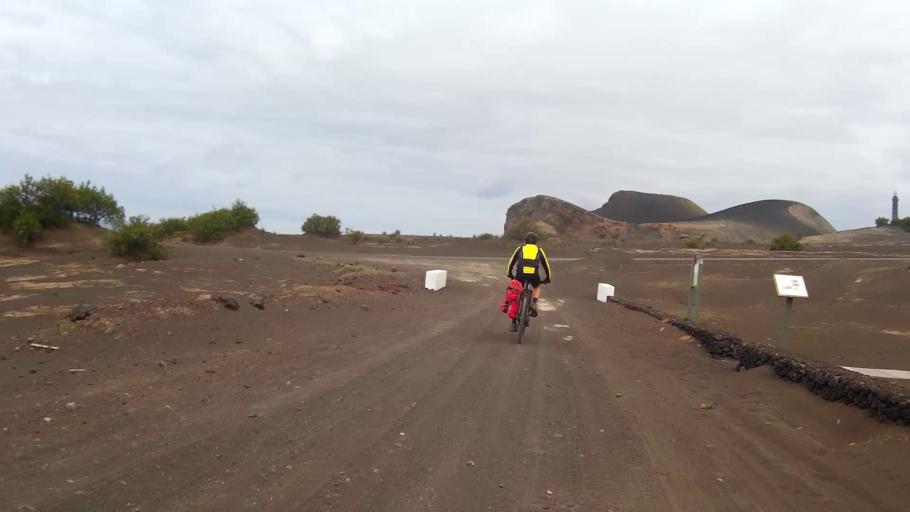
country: PT
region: Azores
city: Ribeira Grande
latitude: 38.5925
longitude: -28.8253
